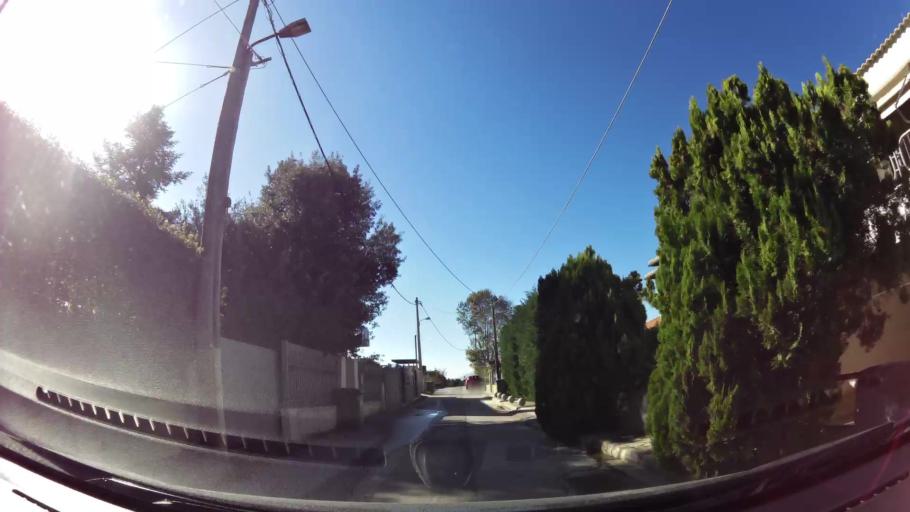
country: GR
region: Attica
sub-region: Nomarchia Anatolikis Attikis
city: Rodopoli
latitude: 38.1201
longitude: 23.8753
